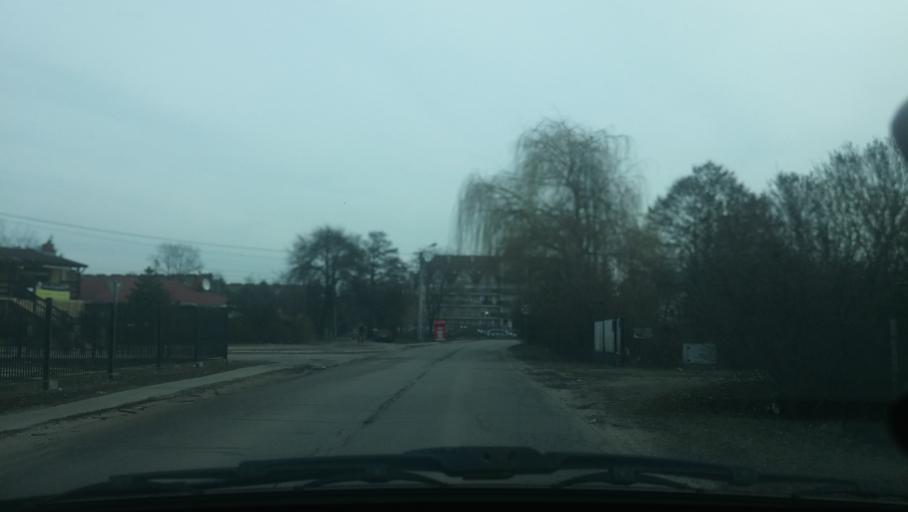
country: PL
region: Masovian Voivodeship
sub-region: Powiat wolominski
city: Zabki
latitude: 52.3050
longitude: 21.0939
